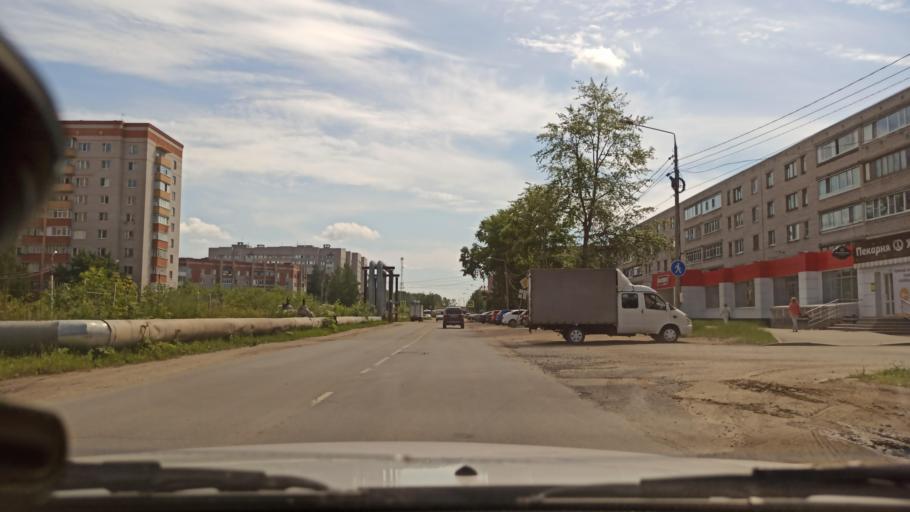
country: RU
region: Vologda
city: Vologda
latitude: 59.1880
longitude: 39.9055
